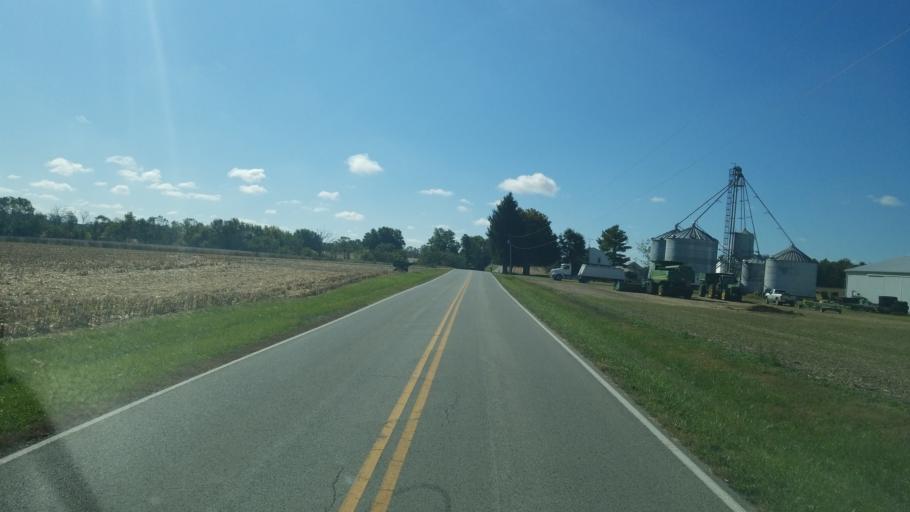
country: US
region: Ohio
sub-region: Highland County
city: Leesburg
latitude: 39.2944
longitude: -83.5797
